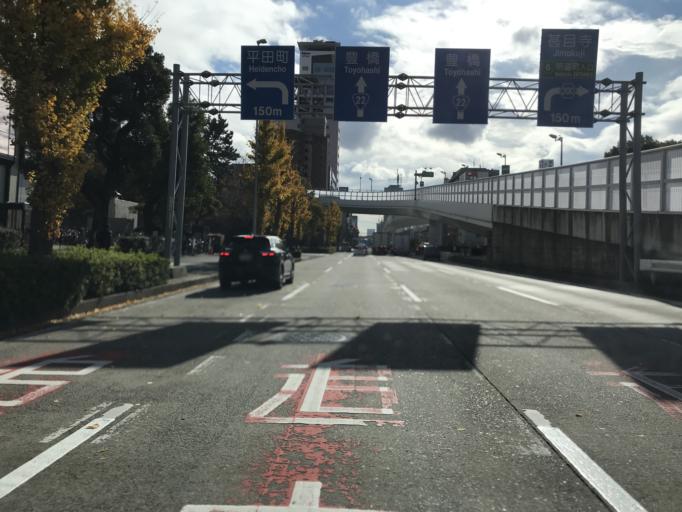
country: JP
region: Aichi
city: Nagoya-shi
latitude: 35.1791
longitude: 136.8966
